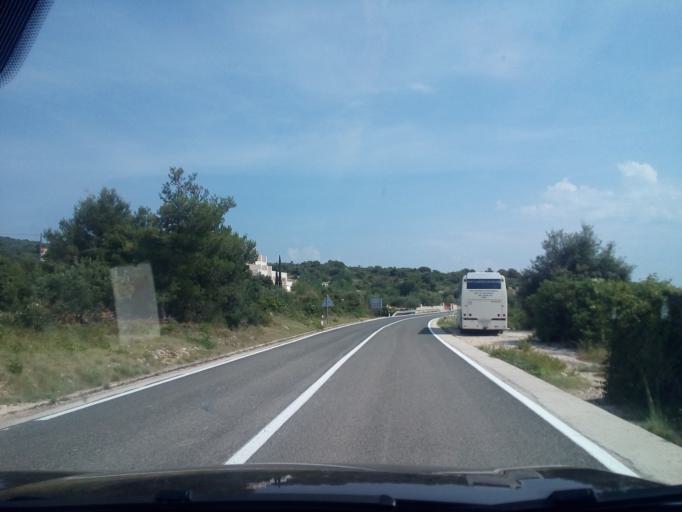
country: HR
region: Sibensko-Kniniska
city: Primosten
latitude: 43.6043
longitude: 15.9214
